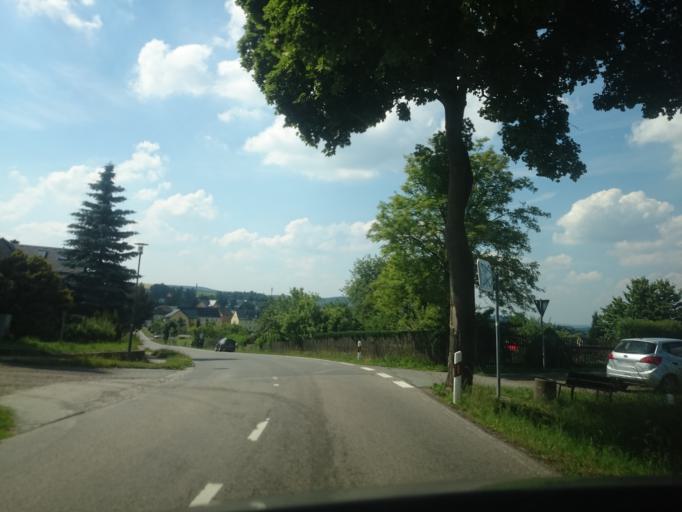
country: DE
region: Saxony
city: Lengefeld
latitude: 50.7144
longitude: 13.2019
